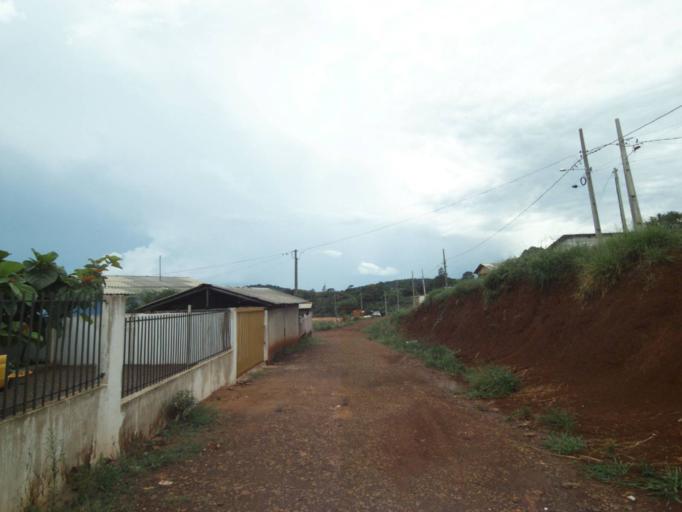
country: BR
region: Parana
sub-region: Guaraniacu
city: Guaraniacu
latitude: -25.0935
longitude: -52.8713
